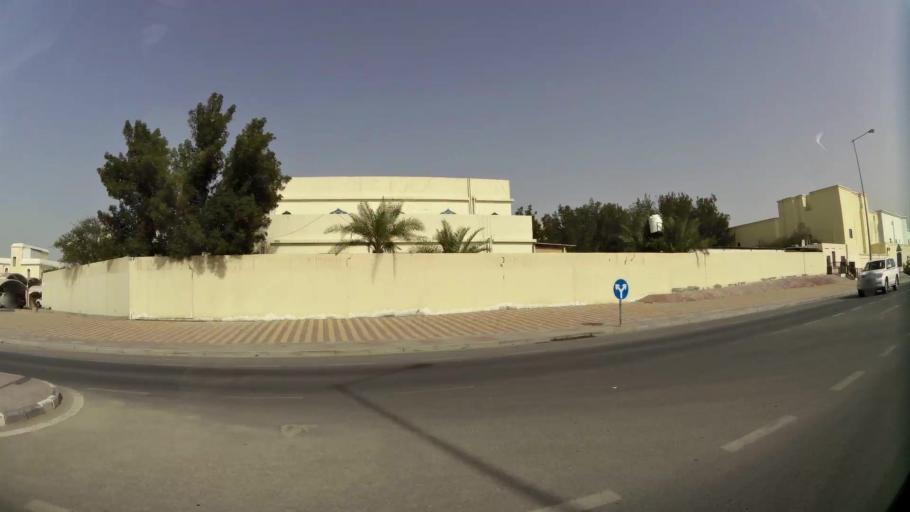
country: QA
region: Baladiyat ar Rayyan
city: Ar Rayyan
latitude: 25.2468
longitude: 51.4436
